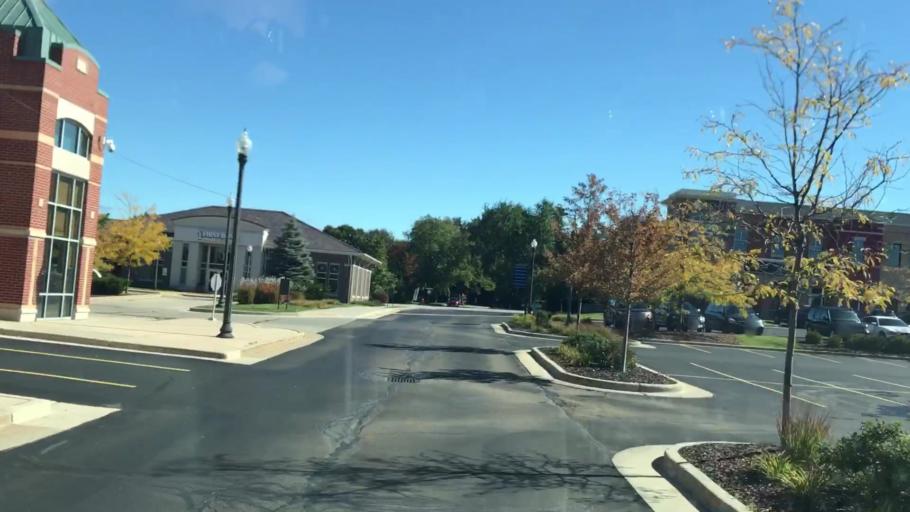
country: US
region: Wisconsin
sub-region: Waukesha County
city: Brookfield
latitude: 43.0893
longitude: -88.1476
